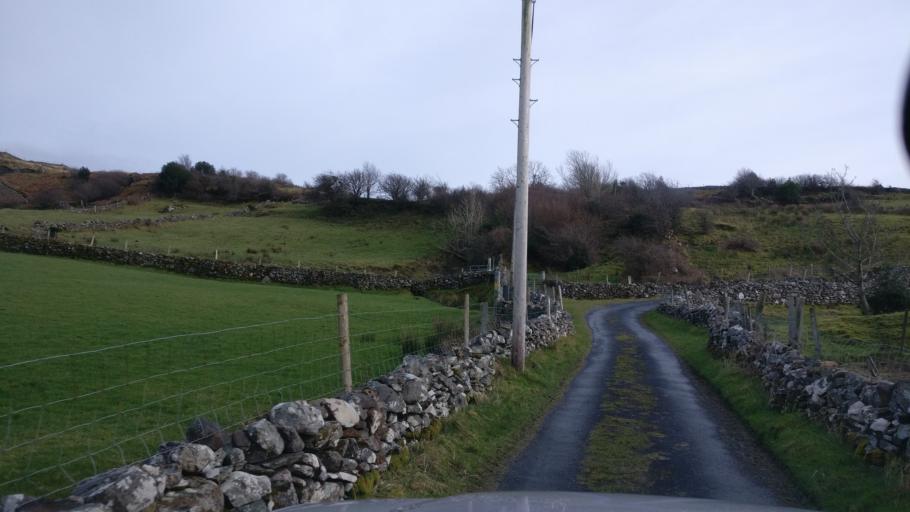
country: IE
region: Connaught
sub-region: County Galway
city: Oughterard
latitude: 53.5550
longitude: -9.4412
